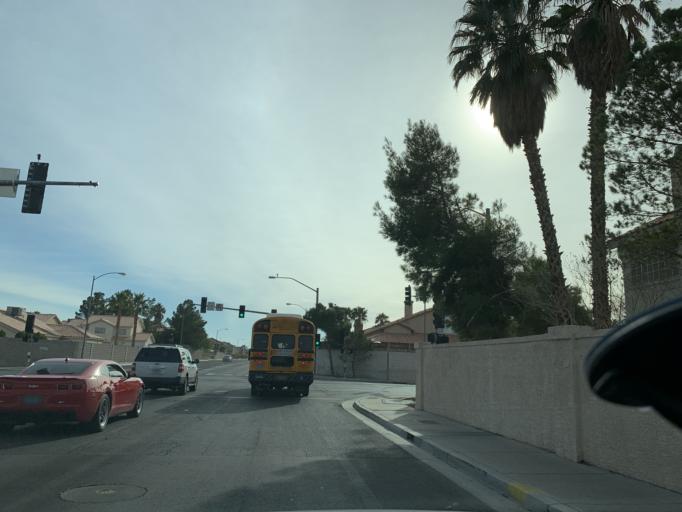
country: US
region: Nevada
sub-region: Clark County
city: Spring Valley
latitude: 36.0929
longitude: -115.2342
